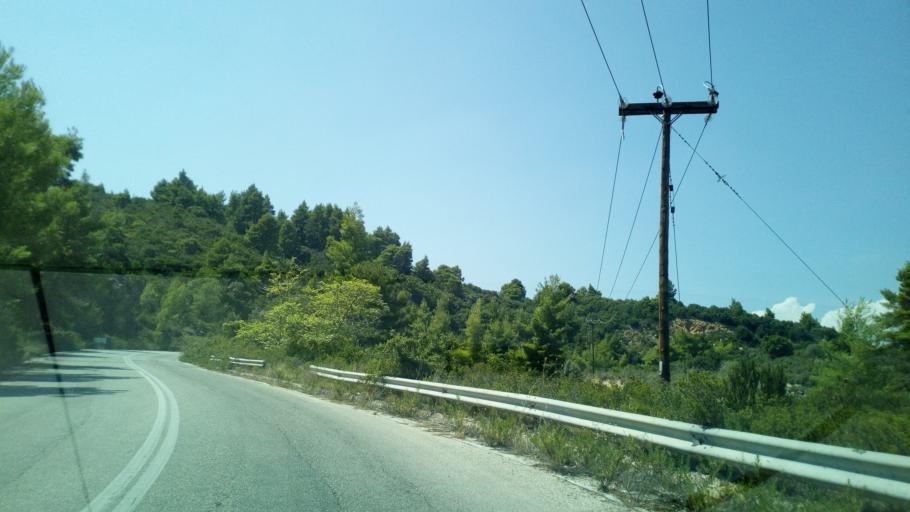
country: GR
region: Central Macedonia
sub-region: Nomos Chalkidikis
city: Sarti
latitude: 40.1590
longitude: 23.8918
